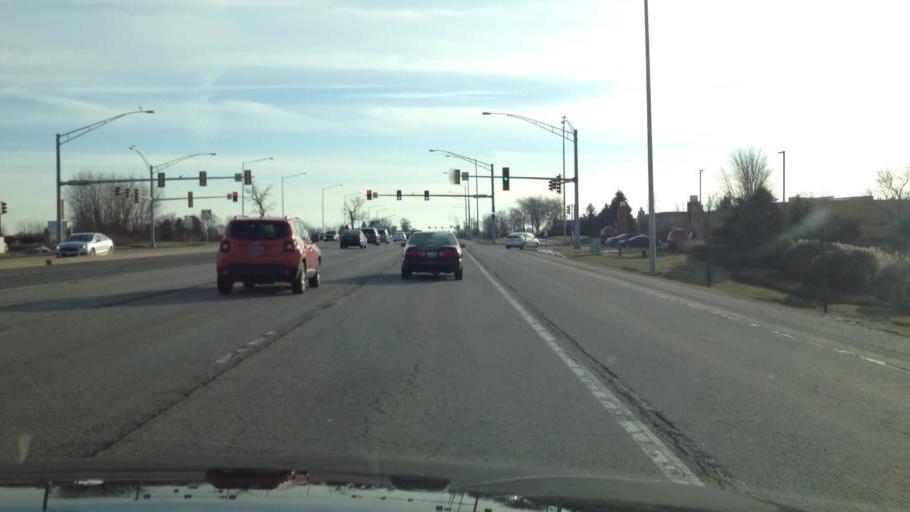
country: US
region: Illinois
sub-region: McHenry County
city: Lake in the Hills
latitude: 42.1514
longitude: -88.3358
